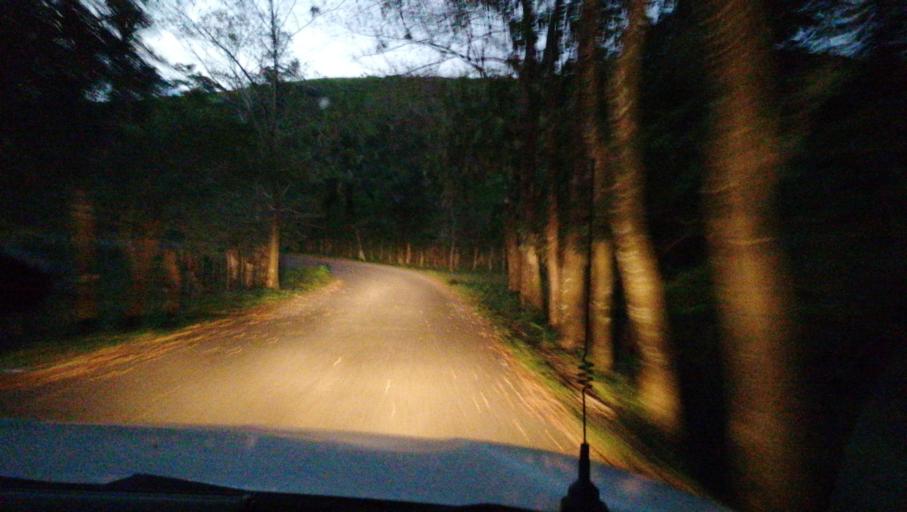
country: MX
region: Chiapas
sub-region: Ostuacan
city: Nuevo Juan del Grijalva
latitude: 17.4817
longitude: -93.3496
